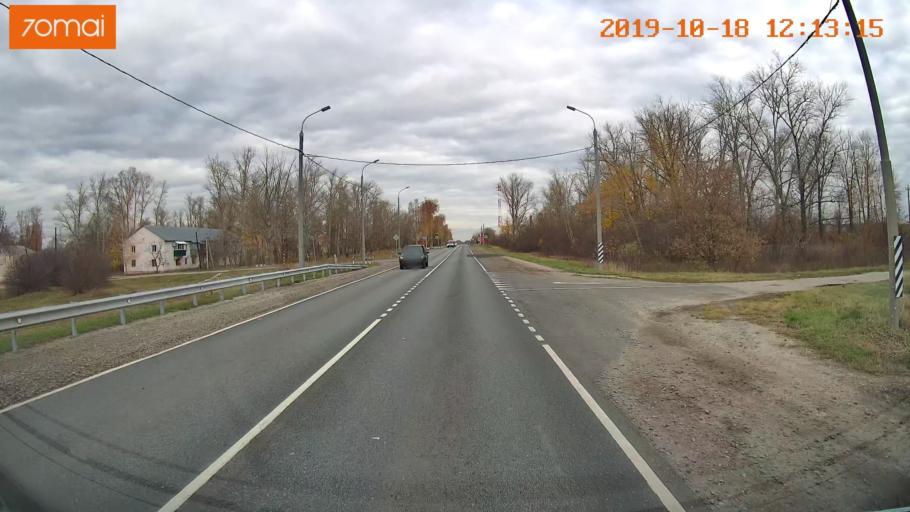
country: RU
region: Rjazan
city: Zakharovo
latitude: 54.4196
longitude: 39.3682
